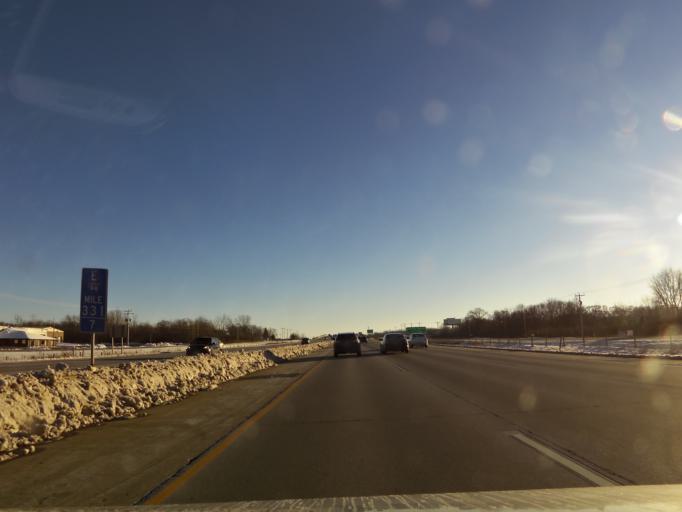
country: US
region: Wisconsin
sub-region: Racine County
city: Franksville
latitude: 42.7482
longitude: -87.9545
